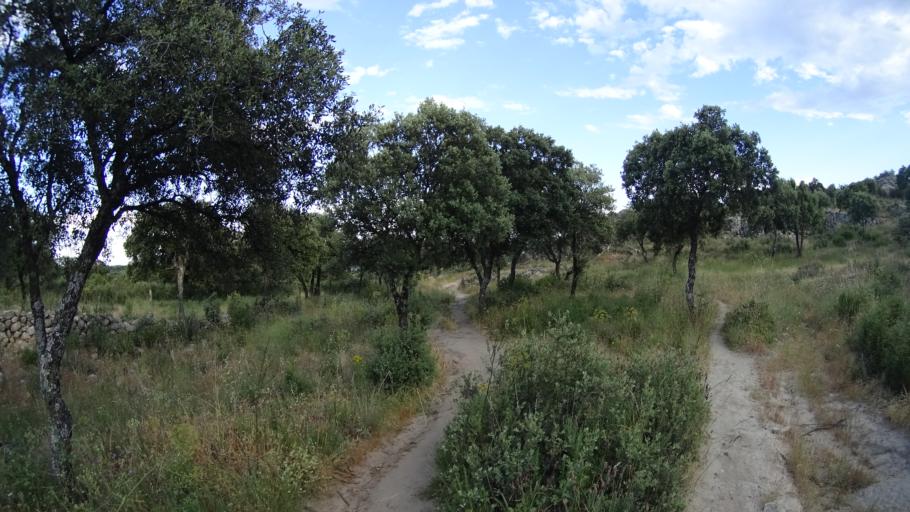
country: ES
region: Madrid
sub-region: Provincia de Madrid
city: Hoyo de Manzanares
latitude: 40.6305
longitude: -3.9121
